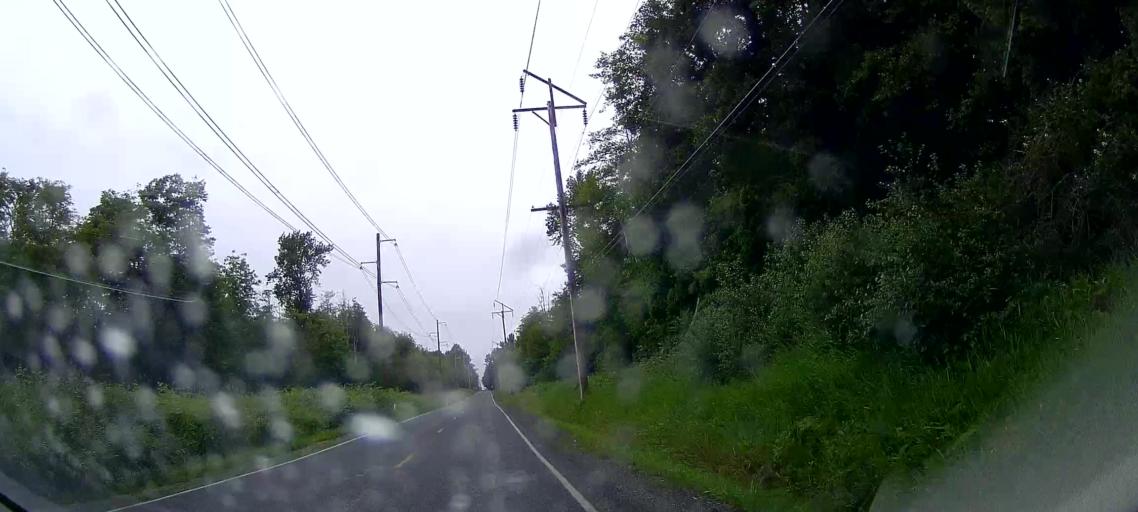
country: US
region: Washington
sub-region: Whatcom County
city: Birch Bay
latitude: 48.8730
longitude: -122.7041
